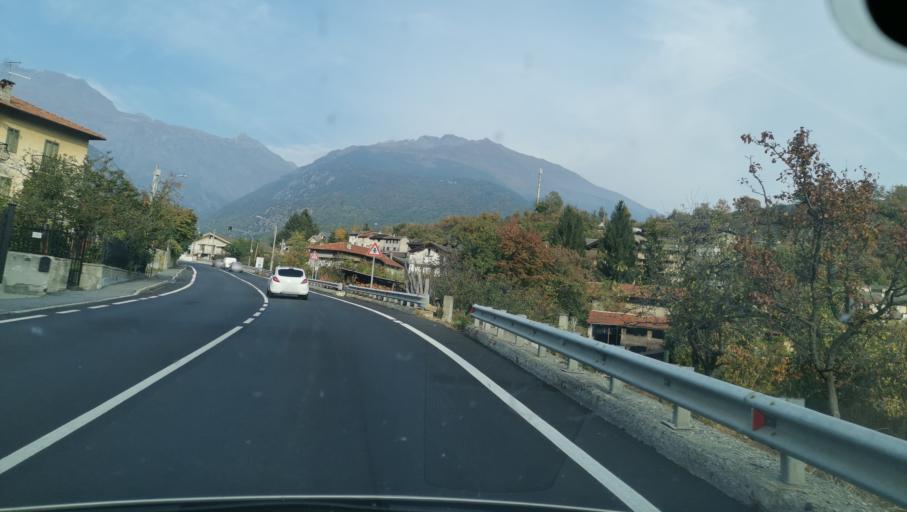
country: IT
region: Piedmont
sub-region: Provincia di Torino
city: Gravere
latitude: 45.1260
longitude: 7.0204
